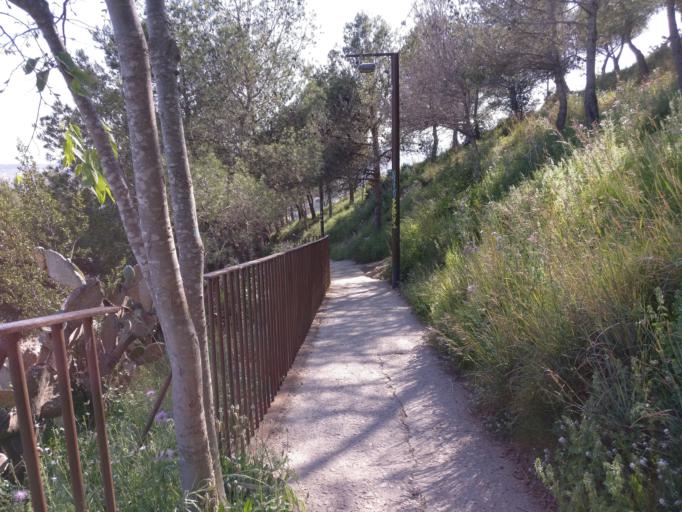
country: ES
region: Catalonia
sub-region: Provincia de Barcelona
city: Horta-Guinardo
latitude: 41.4188
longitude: 2.1615
